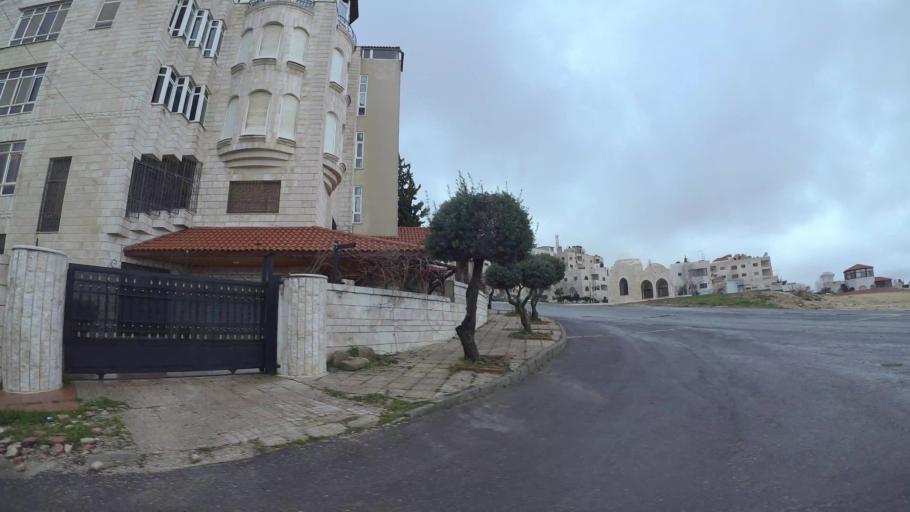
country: JO
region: Amman
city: Al Jubayhah
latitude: 32.0319
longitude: 35.8546
